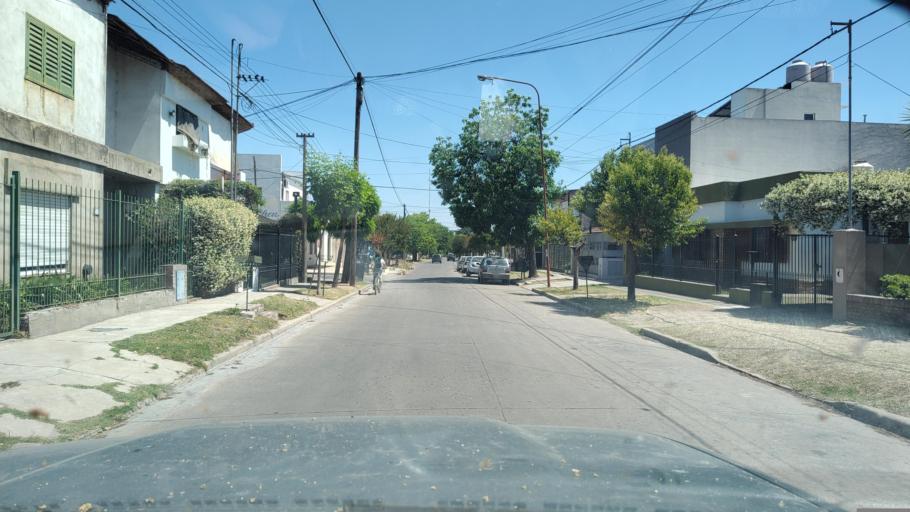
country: AR
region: Buenos Aires
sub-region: Partido de Lujan
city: Lujan
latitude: -34.5816
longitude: -59.1107
